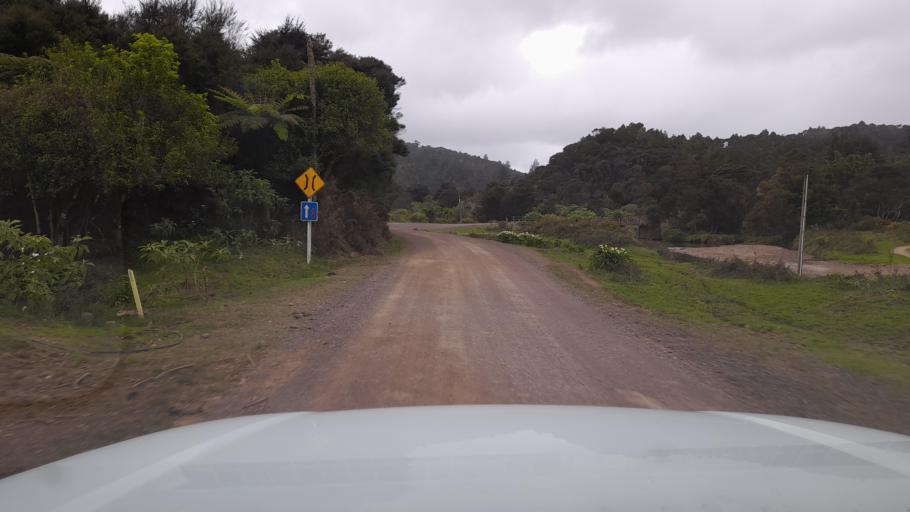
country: NZ
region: Northland
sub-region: Far North District
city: Paihia
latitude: -35.3536
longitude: 174.2289
